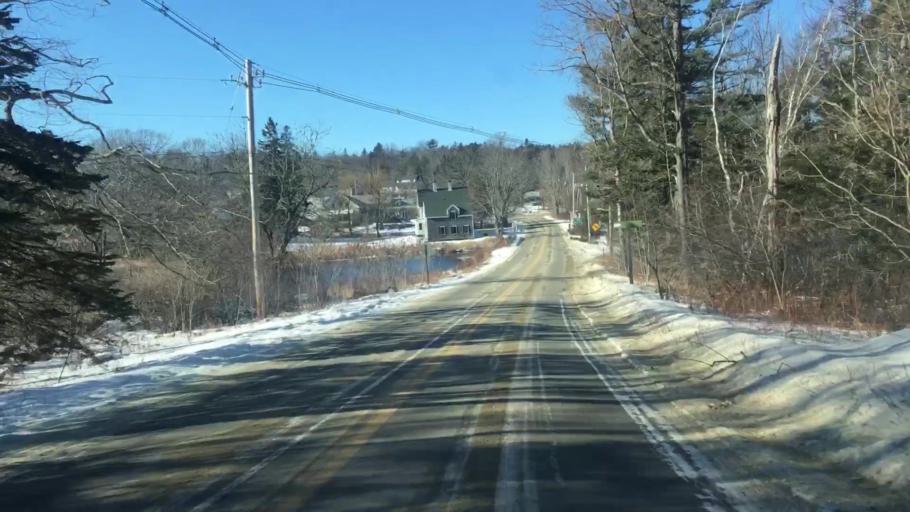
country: US
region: Maine
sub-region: Hancock County
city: Sedgwick
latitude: 44.3457
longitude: -68.6818
